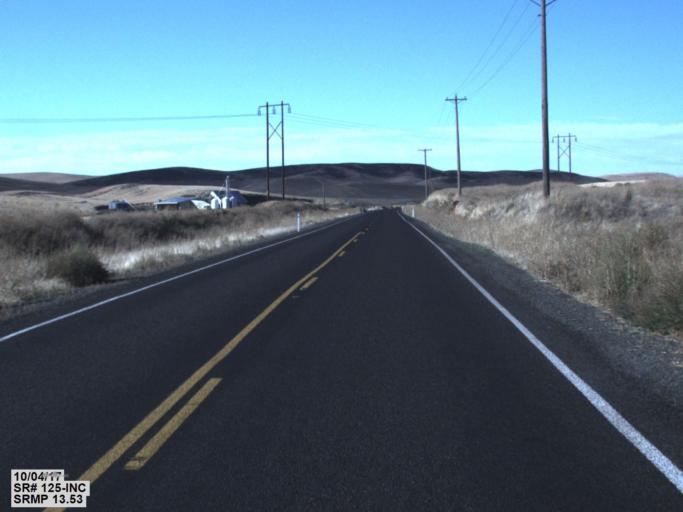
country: US
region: Washington
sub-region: Walla Walla County
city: Walla Walla
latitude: 46.1651
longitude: -118.3806
